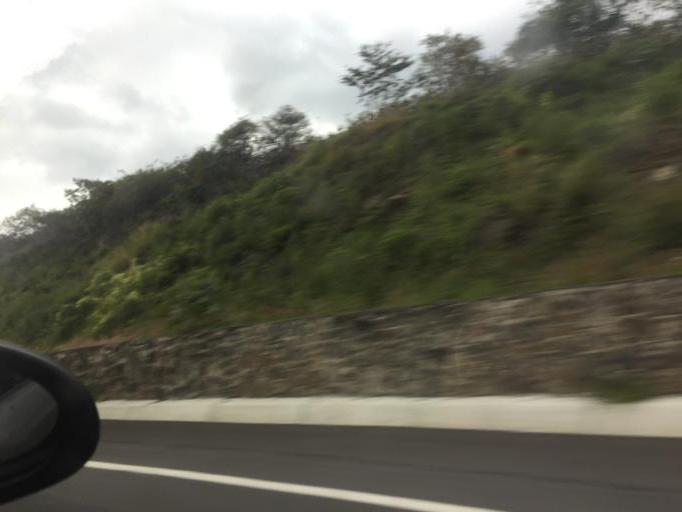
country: MX
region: Jalisco
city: Ocotlan
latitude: 20.4276
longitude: -102.7760
